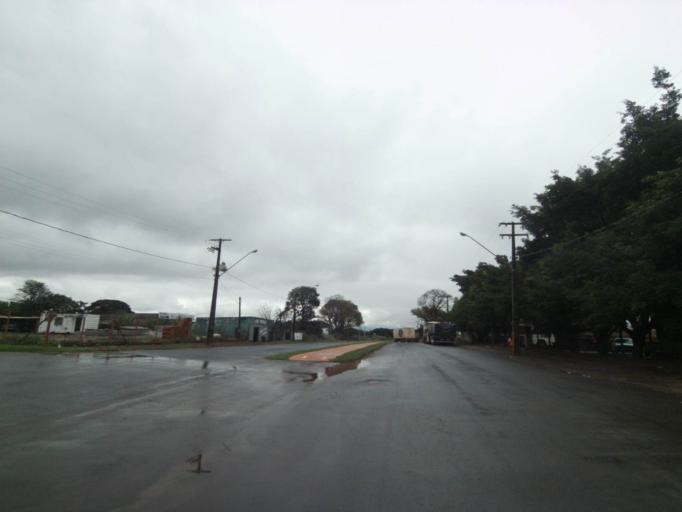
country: BR
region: Parana
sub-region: Foz Do Iguacu
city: Foz do Iguacu
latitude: -25.5134
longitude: -54.5613
